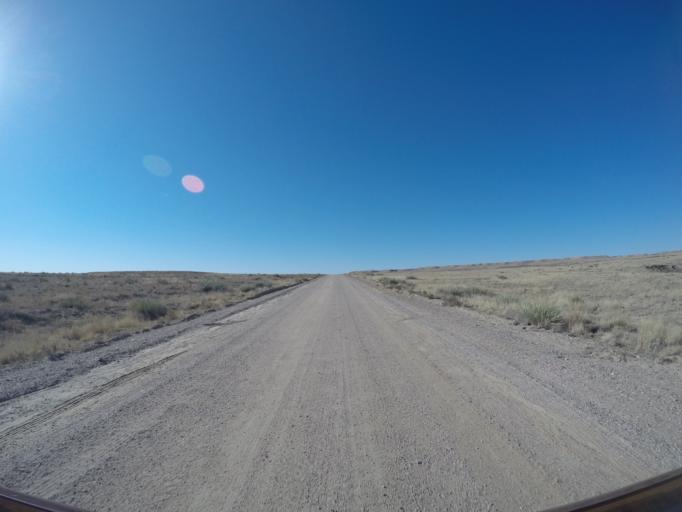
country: US
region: Colorado
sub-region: Otero County
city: La Junta
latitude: 37.7720
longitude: -103.5599
